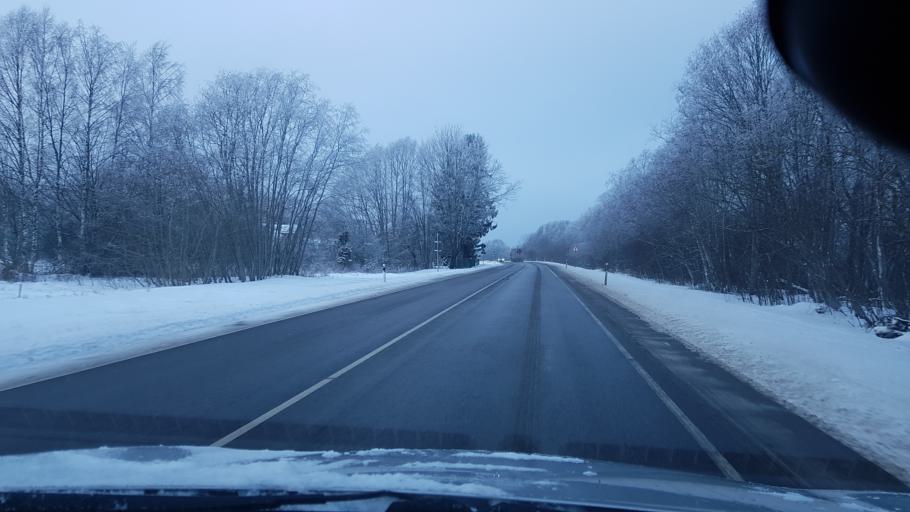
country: EE
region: Harju
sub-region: Paldiski linn
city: Paldiski
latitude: 59.3411
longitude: 24.1995
